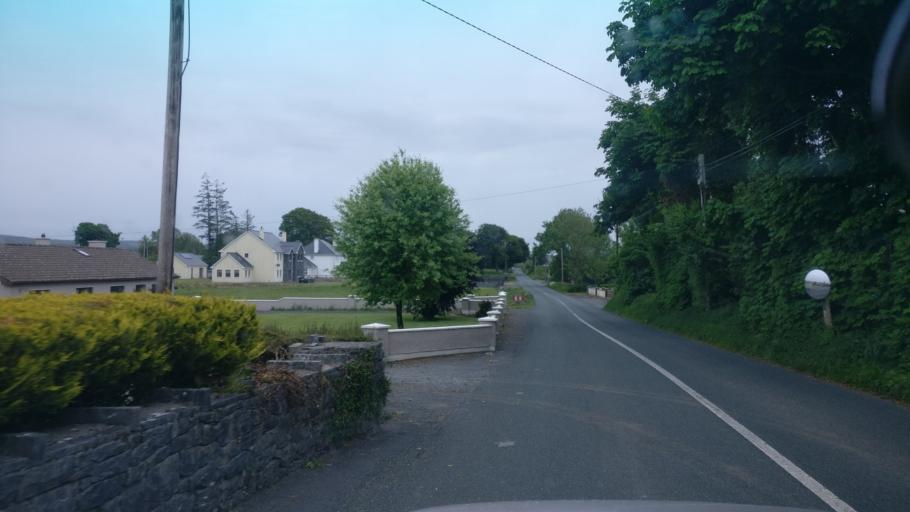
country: IE
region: Connaught
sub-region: County Galway
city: Gort
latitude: 53.0674
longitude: -8.7801
